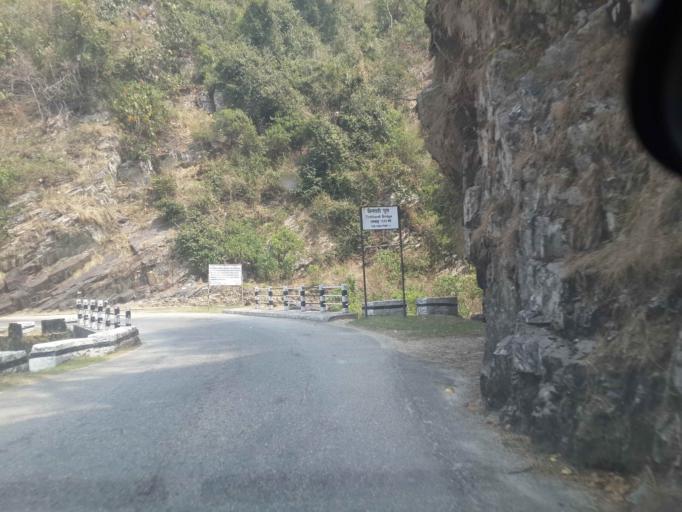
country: NP
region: Central Region
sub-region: Narayani Zone
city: Hitura
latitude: 27.4972
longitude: 85.0451
